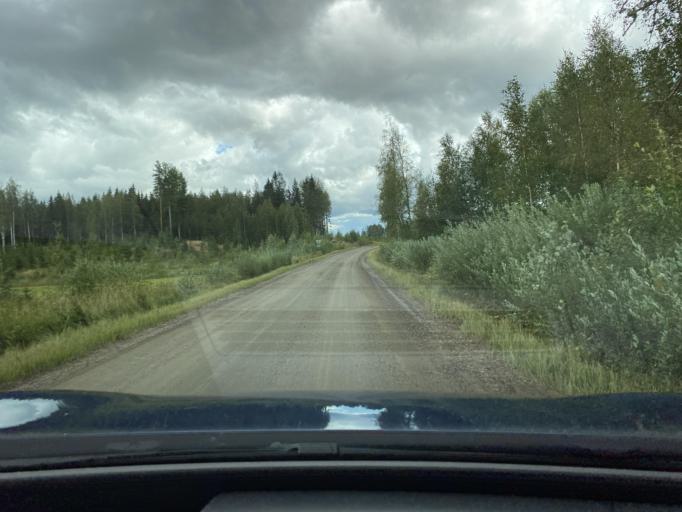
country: FI
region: Pirkanmaa
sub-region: Lounais-Pirkanmaa
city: Punkalaidun
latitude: 61.2317
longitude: 23.1493
